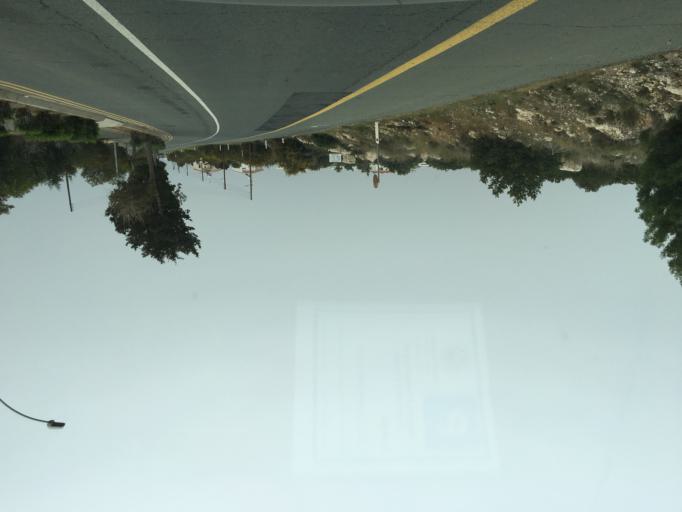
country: CY
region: Ammochostos
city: Ayia Napa
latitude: 34.9894
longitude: 34.0079
